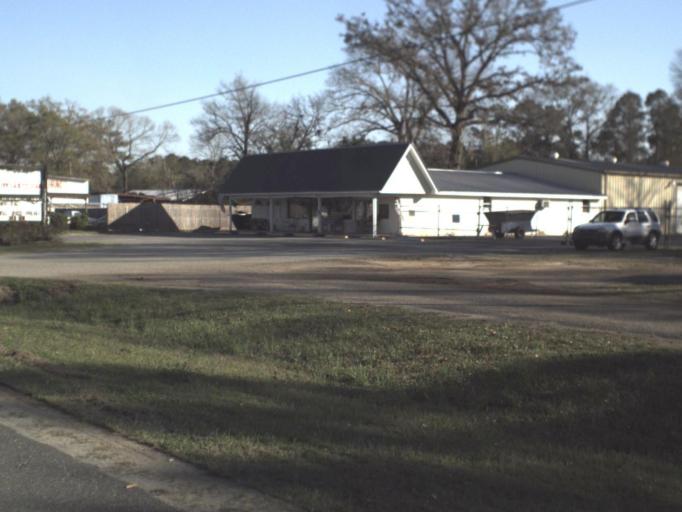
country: US
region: Florida
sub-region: Jackson County
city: Sneads
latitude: 30.7099
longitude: -84.9141
